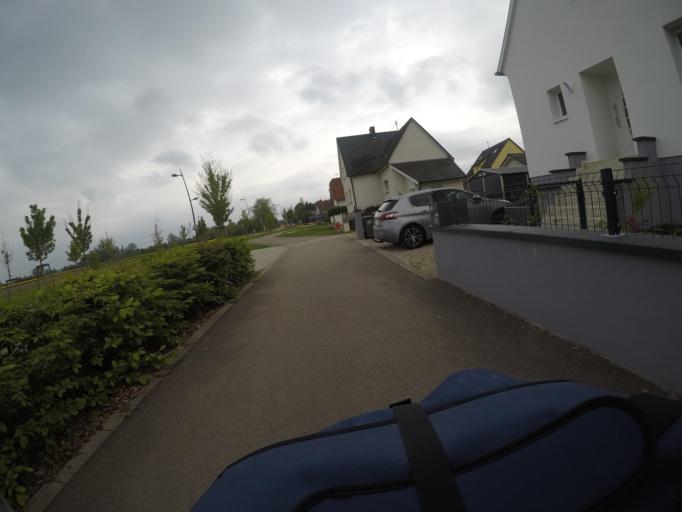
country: FR
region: Alsace
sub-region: Departement du Bas-Rhin
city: Gambsheim
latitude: 48.6900
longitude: 7.8945
